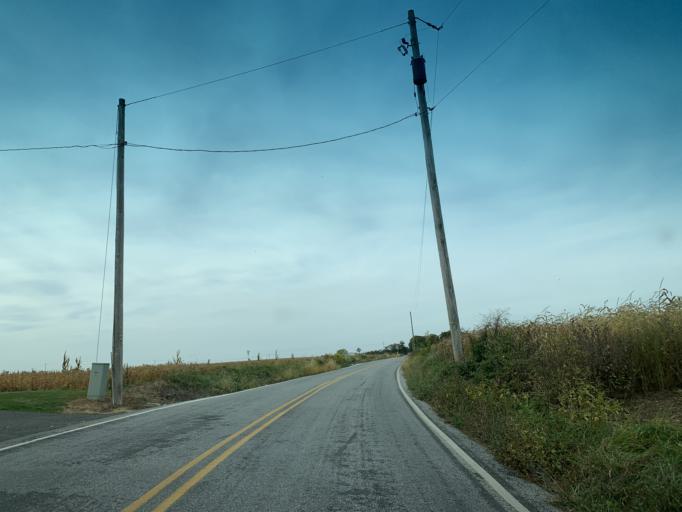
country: US
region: Pennsylvania
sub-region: York County
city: Stewartstown
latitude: 39.8064
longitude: -76.5230
